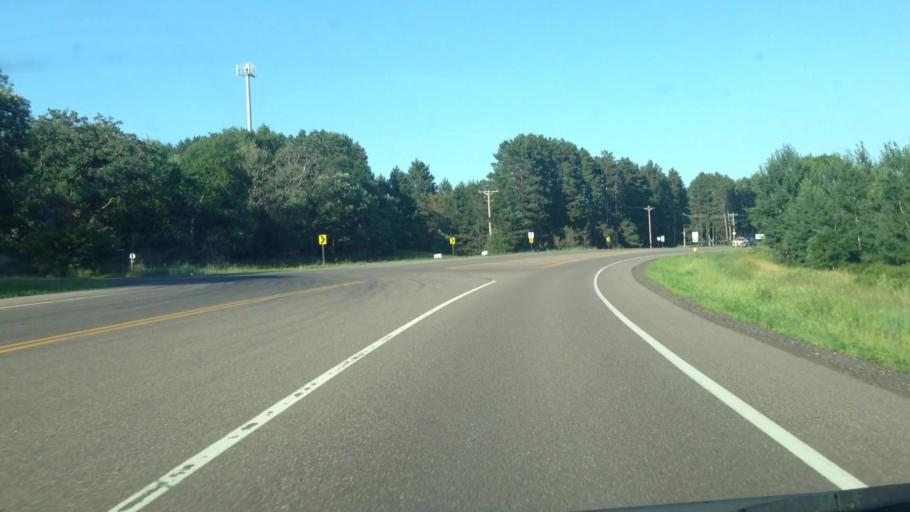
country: US
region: Minnesota
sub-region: Sherburne County
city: Zimmerman
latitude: 45.4452
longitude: -93.6399
